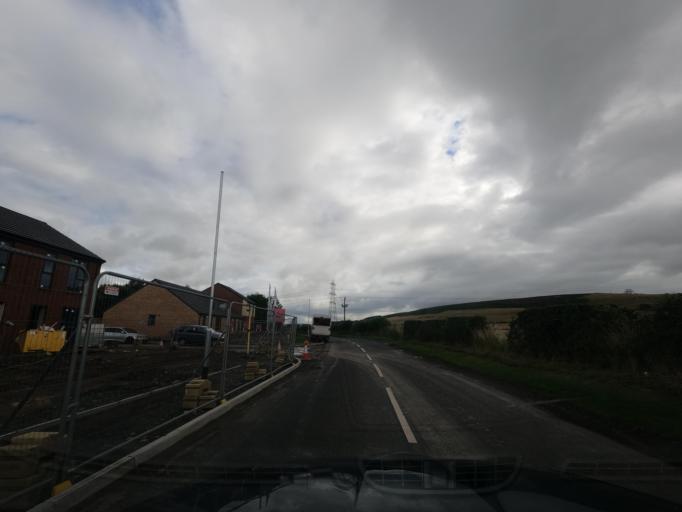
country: GB
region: England
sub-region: Northumberland
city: Wooler
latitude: 55.5482
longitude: -2.0080
